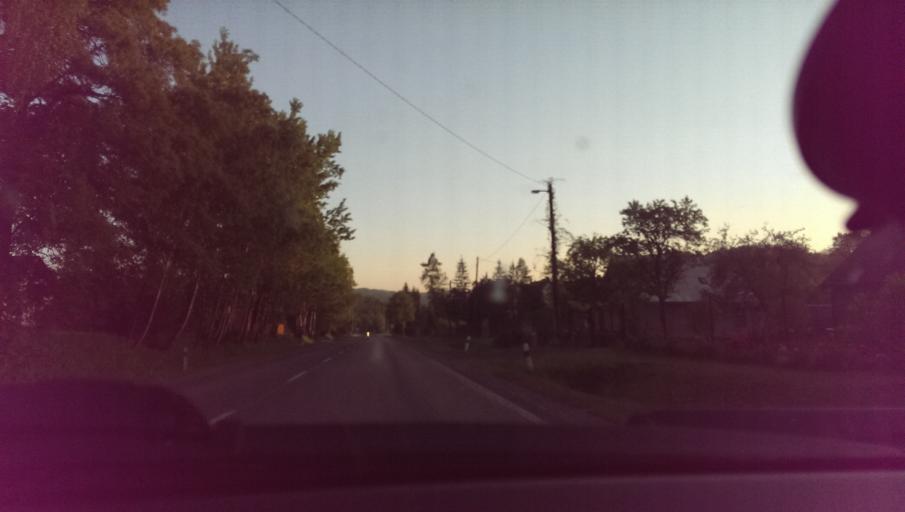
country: CZ
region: Zlin
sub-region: Okres Vsetin
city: Roznov pod Radhostem
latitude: 49.4755
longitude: 18.1638
